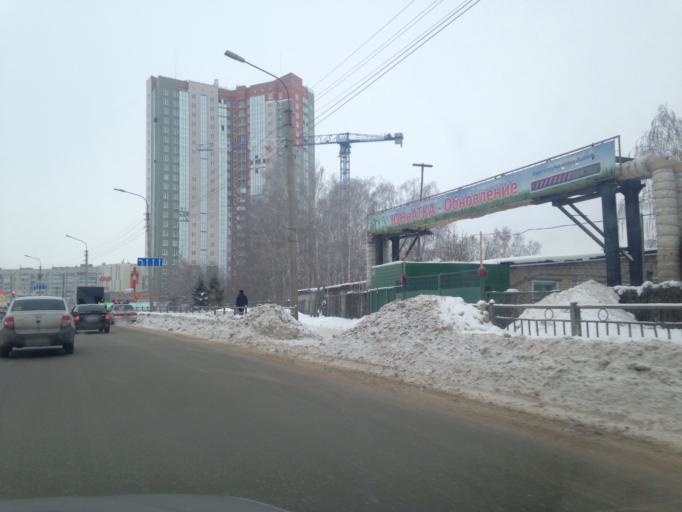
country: RU
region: Ulyanovsk
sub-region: Ulyanovskiy Rayon
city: Ulyanovsk
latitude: 54.3027
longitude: 48.3484
